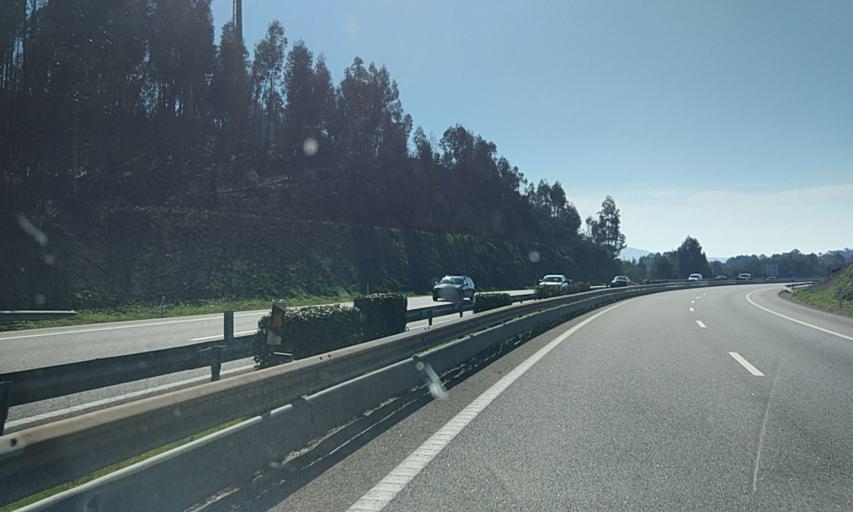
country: PT
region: Porto
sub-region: Paredes
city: Baltar
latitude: 41.1754
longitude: -8.3806
